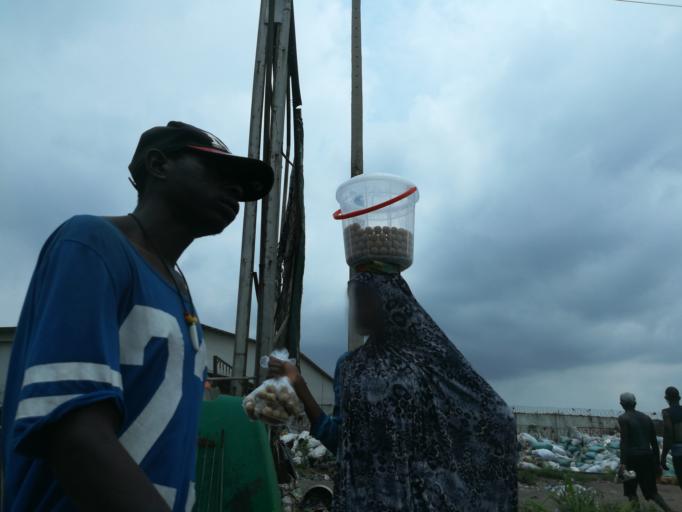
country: NG
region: Lagos
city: Agege
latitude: 6.6117
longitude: 3.3291
